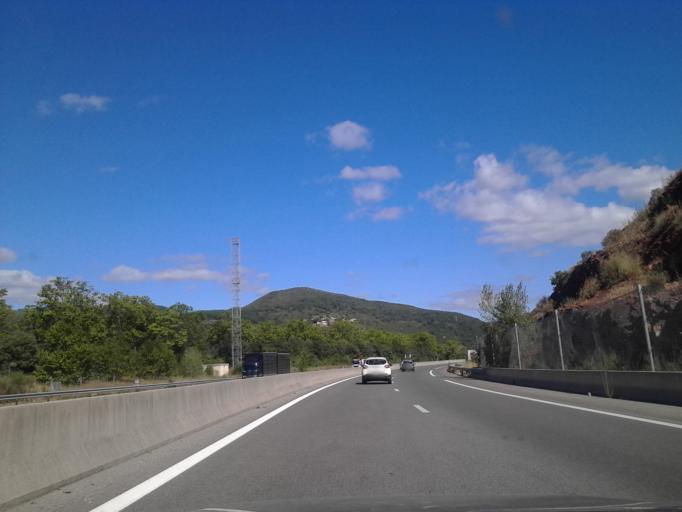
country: FR
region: Languedoc-Roussillon
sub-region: Departement de l'Herault
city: Lodeve
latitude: 43.6994
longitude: 3.3327
